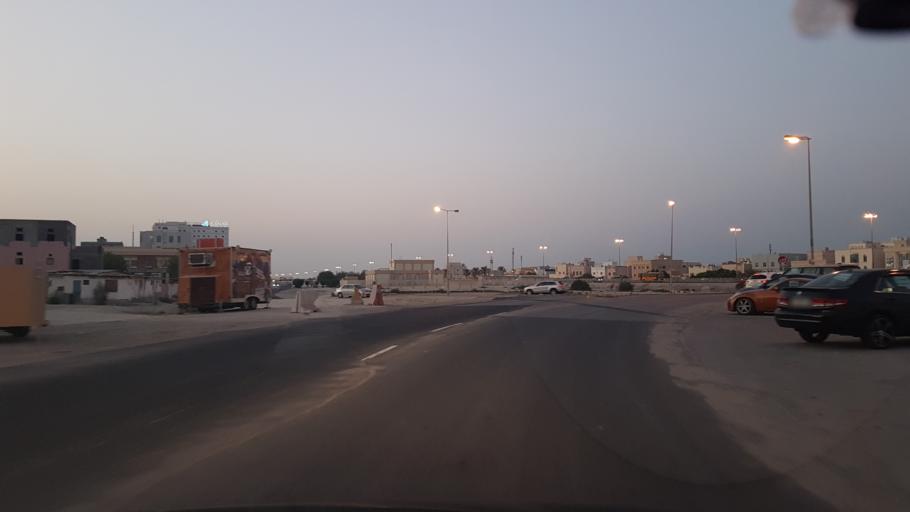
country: BH
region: Northern
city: Ar Rifa'
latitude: 26.1501
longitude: 50.5728
